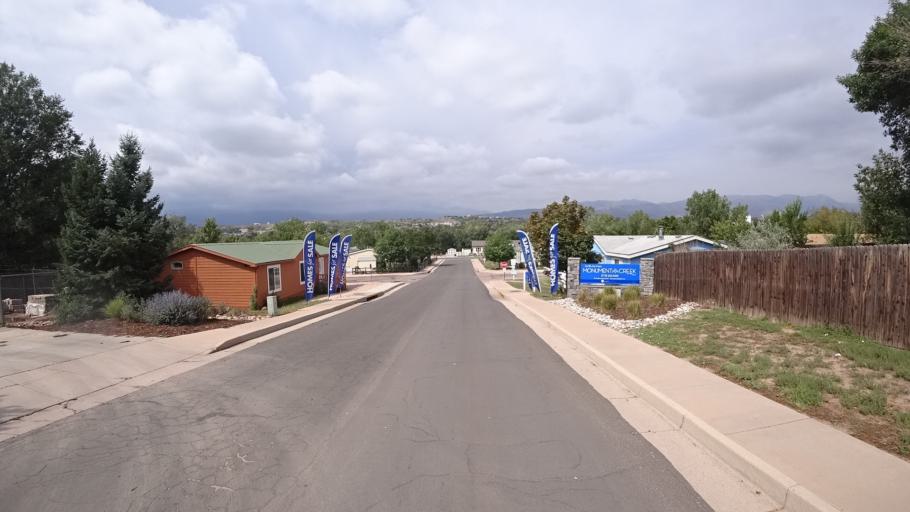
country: US
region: Colorado
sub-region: El Paso County
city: Colorado Springs
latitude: 38.8820
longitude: -104.8265
